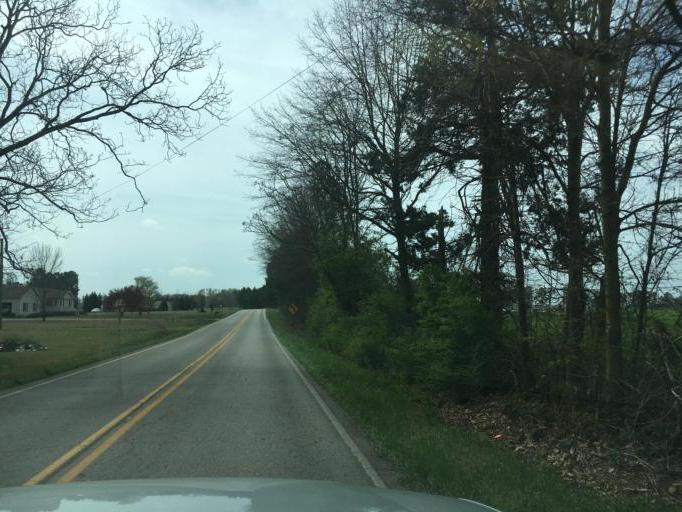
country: US
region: Georgia
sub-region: Hart County
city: Royston
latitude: 34.3106
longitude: -83.0484
